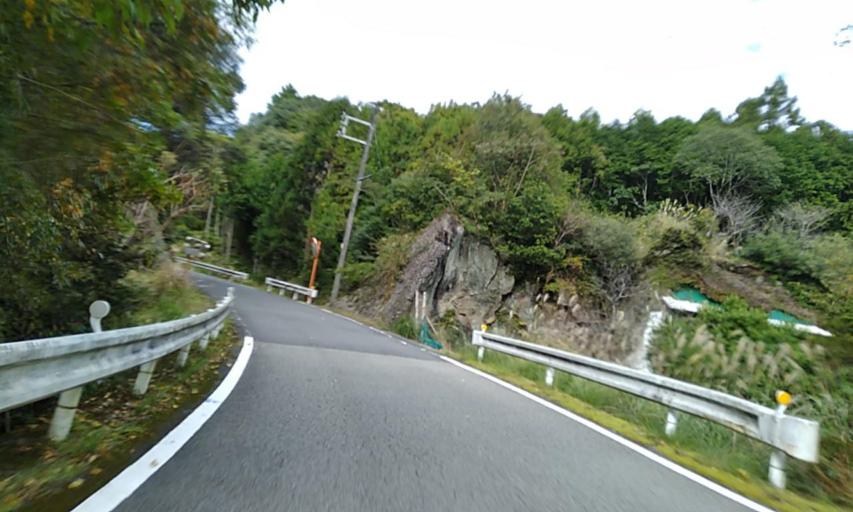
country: JP
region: Wakayama
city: Shingu
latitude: 33.5431
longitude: 135.8455
